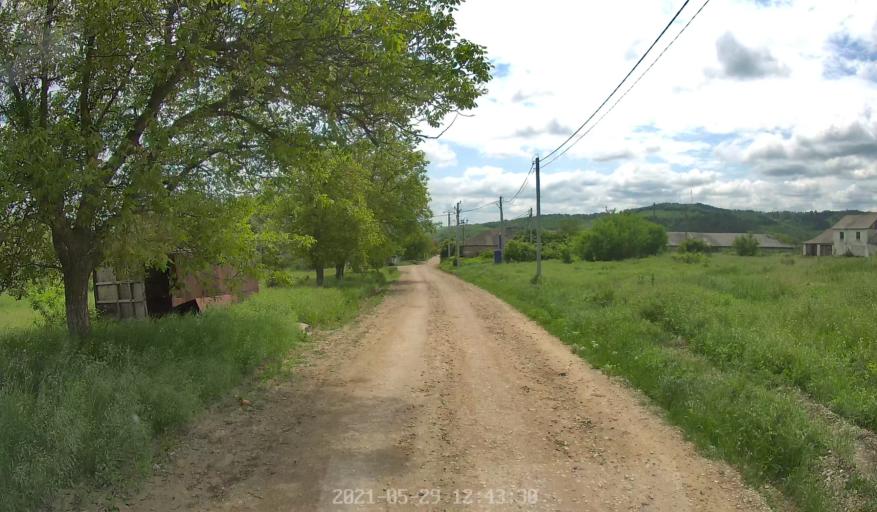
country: MD
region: Hincesti
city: Hincesti
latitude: 46.8741
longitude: 28.6354
